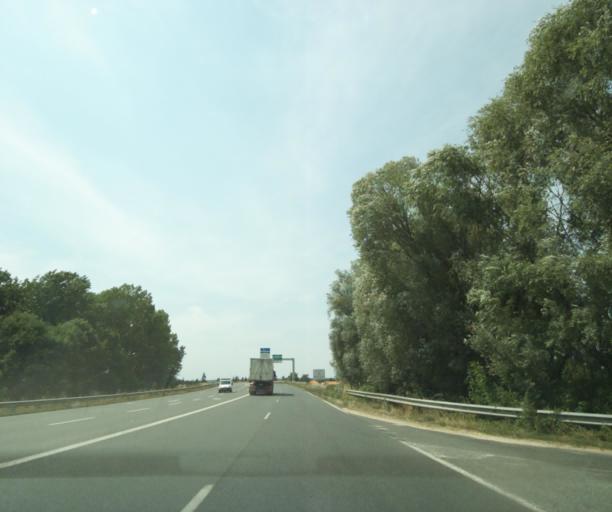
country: FR
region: Poitou-Charentes
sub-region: Departement de la Vienne
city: Antran
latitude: 46.8370
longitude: 0.5524
